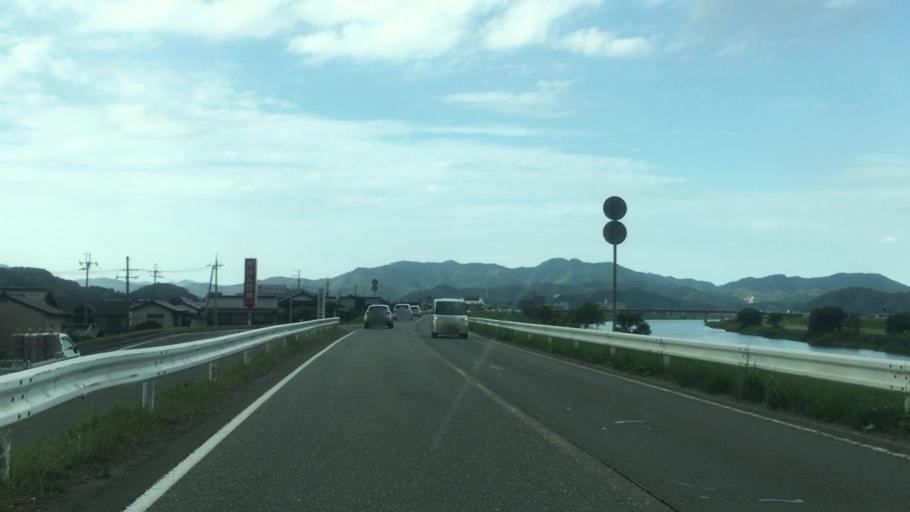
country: JP
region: Hyogo
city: Toyooka
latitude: 35.5176
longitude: 134.8207
